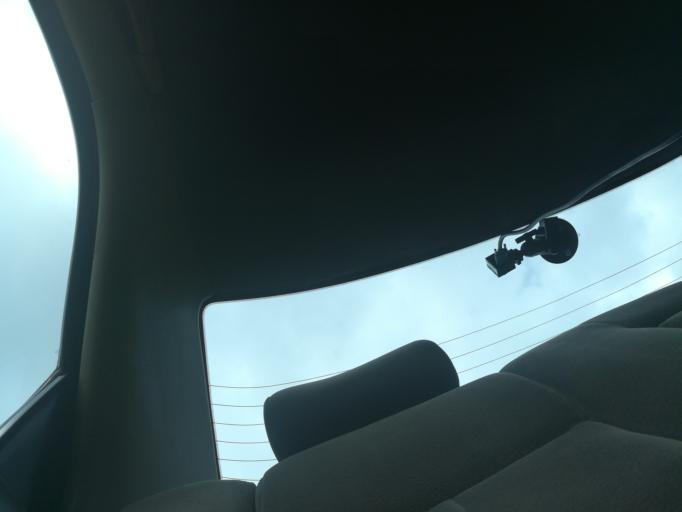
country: NG
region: Lagos
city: Ikorodu
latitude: 6.6556
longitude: 3.5817
